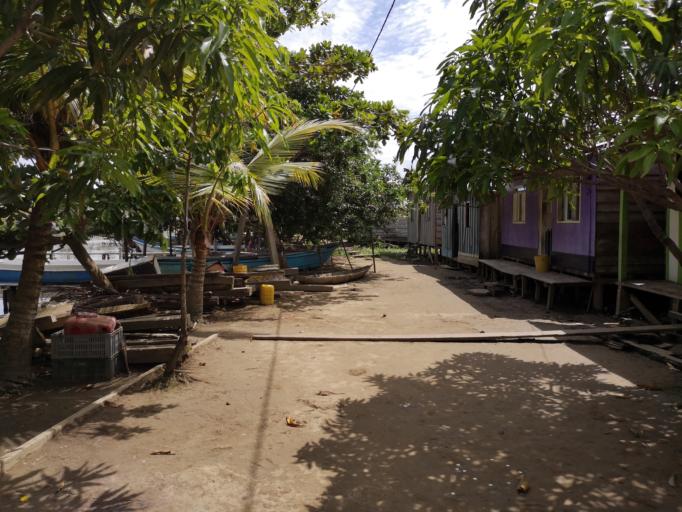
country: CO
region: Antioquia
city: Turbo
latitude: 8.0884
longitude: -76.8359
